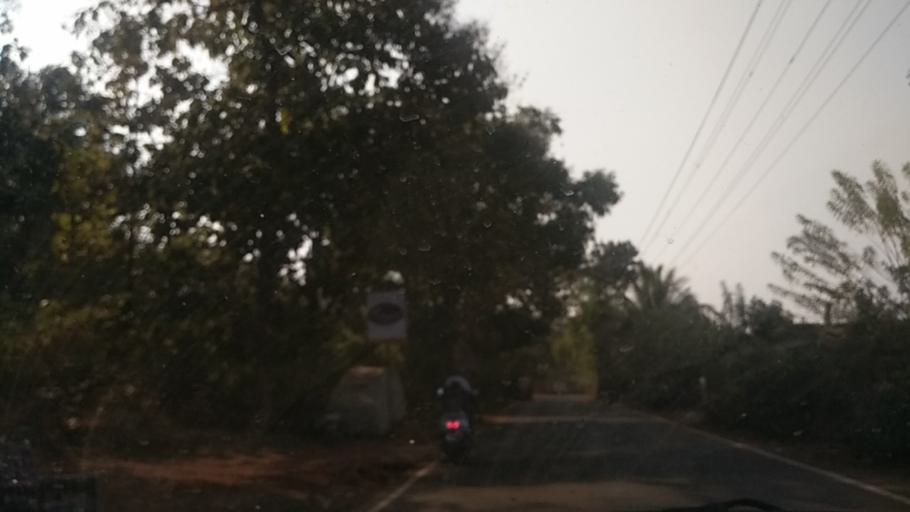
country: IN
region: Goa
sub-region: North Goa
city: Pernem
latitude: 15.7130
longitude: 73.8093
